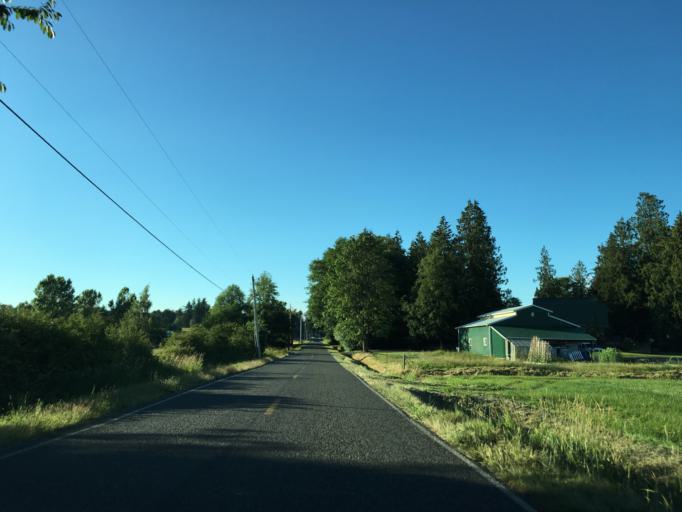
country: US
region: Washington
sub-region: Whatcom County
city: Lynden
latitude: 48.9739
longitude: -122.5299
